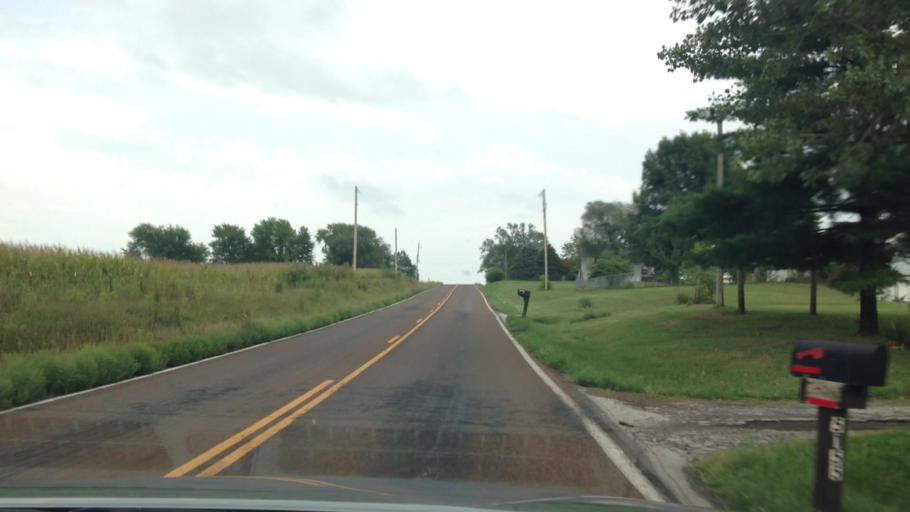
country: US
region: Missouri
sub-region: Clay County
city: Smithville
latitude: 39.4050
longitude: -94.6384
